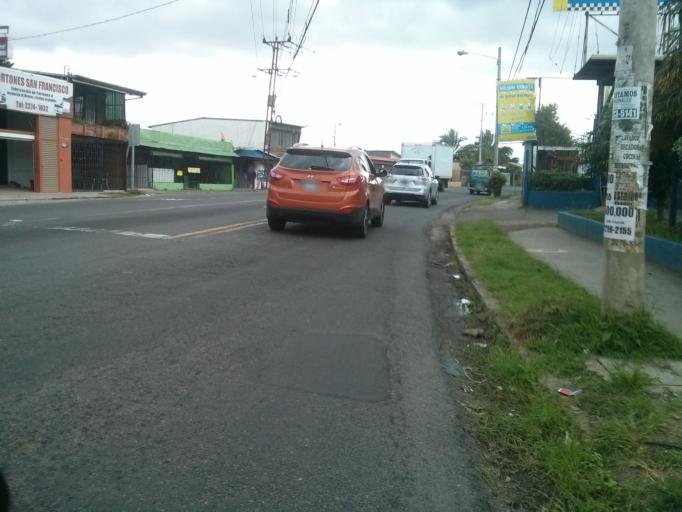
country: CR
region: San Jose
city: Curridabat
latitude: 9.9038
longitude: -84.0450
